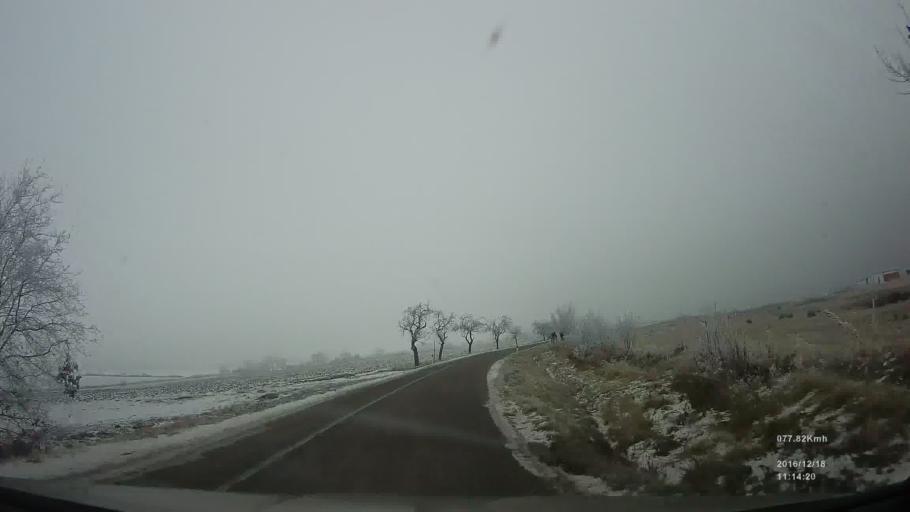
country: SK
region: Presovsky
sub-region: Okres Presov
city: Presov
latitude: 48.8925
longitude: 21.3162
